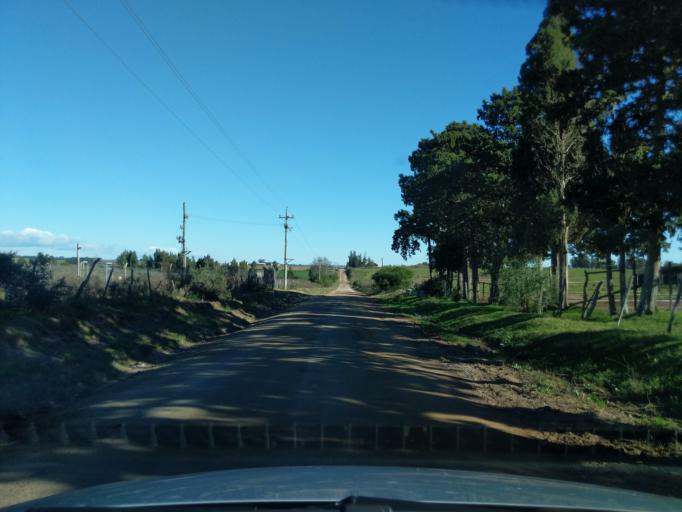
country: UY
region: Florida
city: Florida
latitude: -34.0841
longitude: -56.2423
